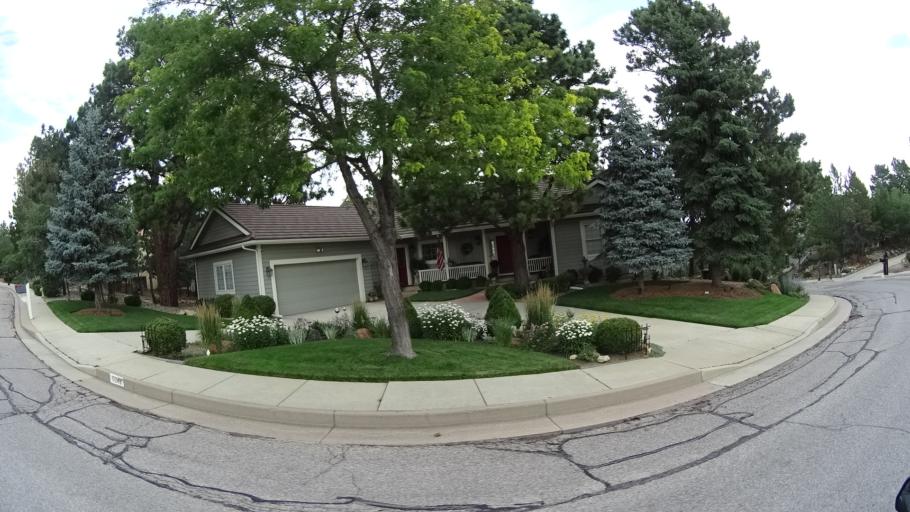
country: US
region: Colorado
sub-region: El Paso County
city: Colorado Springs
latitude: 38.9076
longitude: -104.8478
